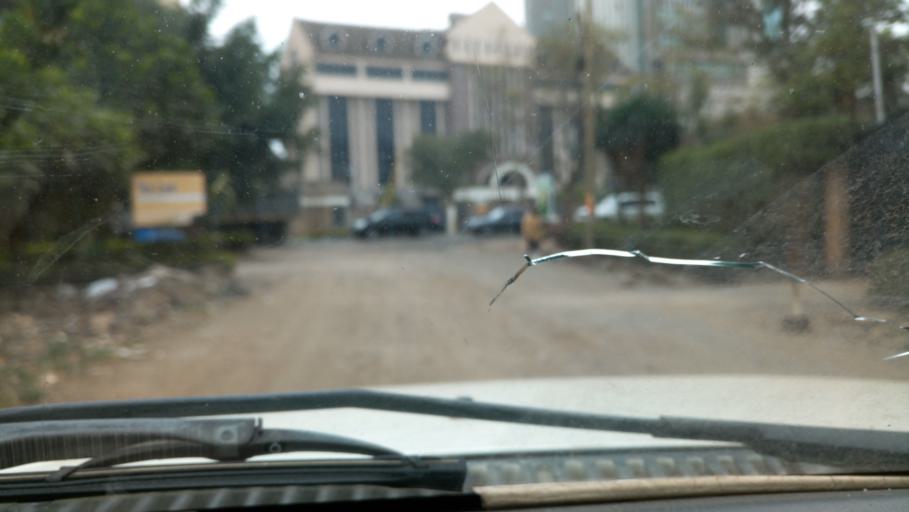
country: KE
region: Nairobi Area
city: Nairobi
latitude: -1.2888
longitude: 36.7879
